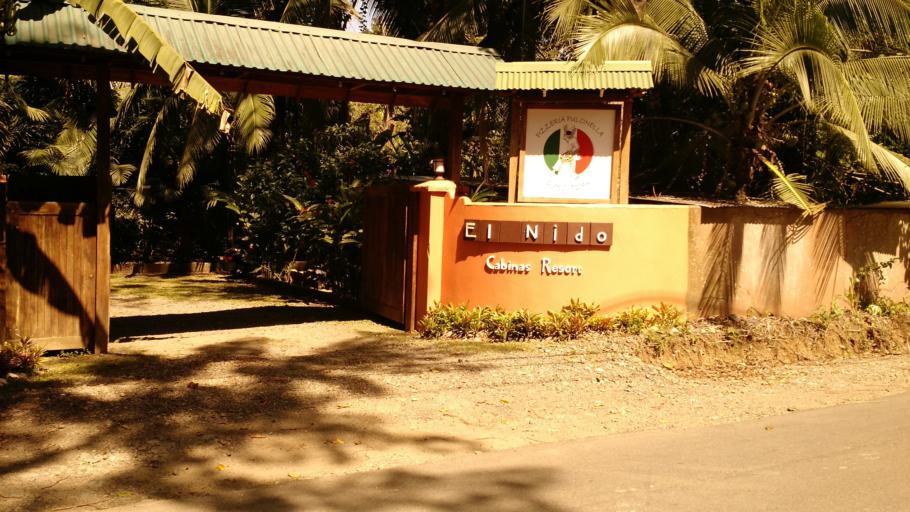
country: PA
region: Bocas del Toro
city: Barranco
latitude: 9.6381
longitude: -82.7116
